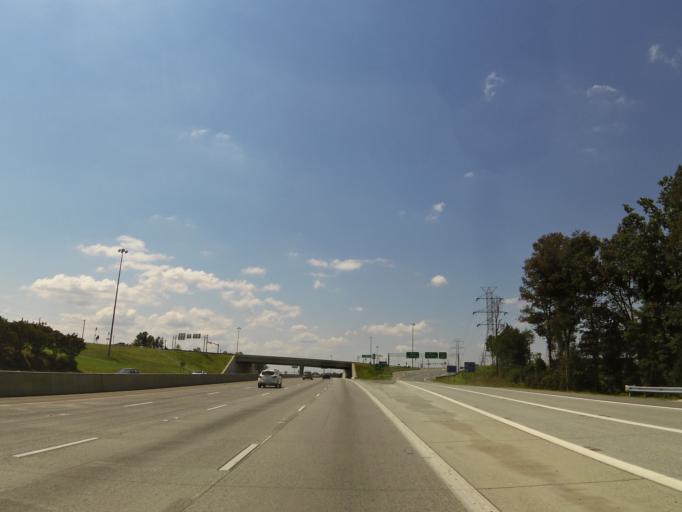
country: US
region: North Carolina
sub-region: Cabarrus County
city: Kannapolis
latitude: 35.4367
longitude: -80.6549
